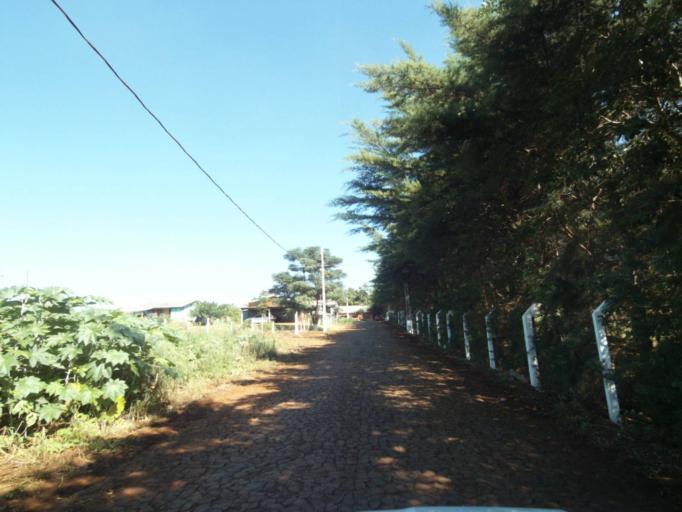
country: BR
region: Parana
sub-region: Laranjeiras Do Sul
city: Laranjeiras do Sul
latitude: -25.4847
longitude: -52.5226
